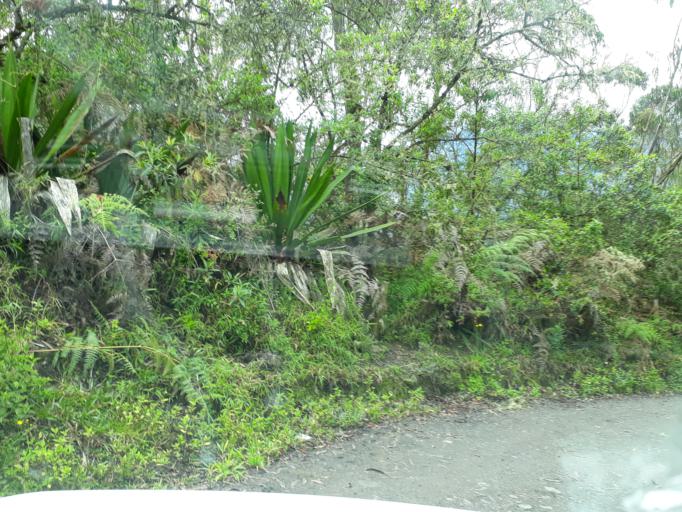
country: CO
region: Cundinamarca
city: Junin
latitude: 4.7963
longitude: -73.6550
